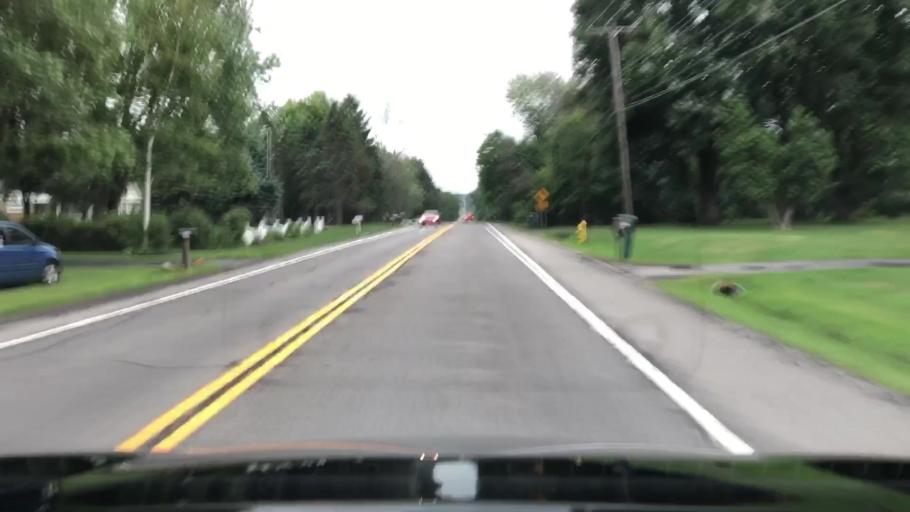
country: US
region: New York
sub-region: Erie County
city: Orchard Park
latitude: 42.7870
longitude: -78.6969
